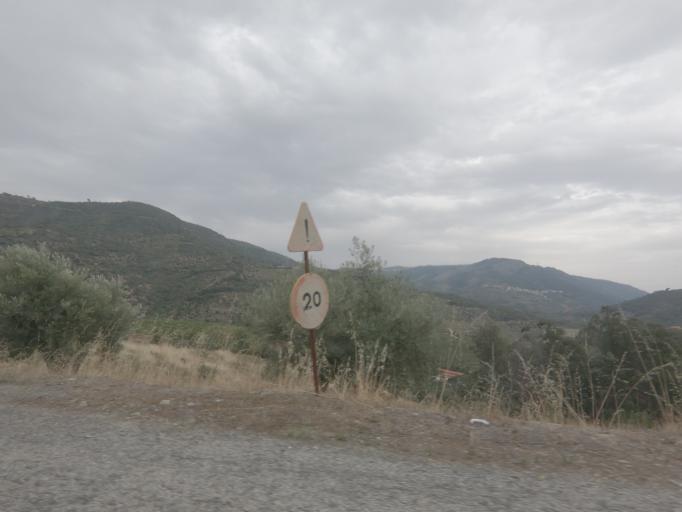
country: PT
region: Viseu
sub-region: Armamar
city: Armamar
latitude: 41.1464
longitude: -7.6448
